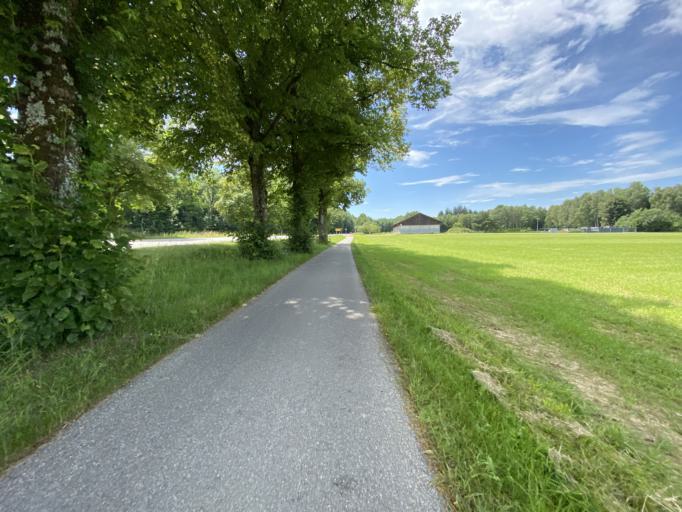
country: DE
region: Bavaria
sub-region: Upper Bavaria
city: Puchheim
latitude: 48.1138
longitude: 11.3346
